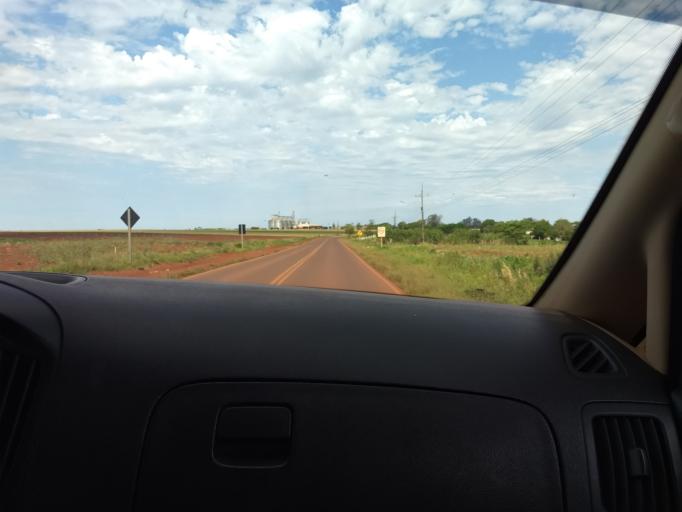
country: PY
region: Alto Parana
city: Santa Rita
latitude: -25.8046
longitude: -55.0579
